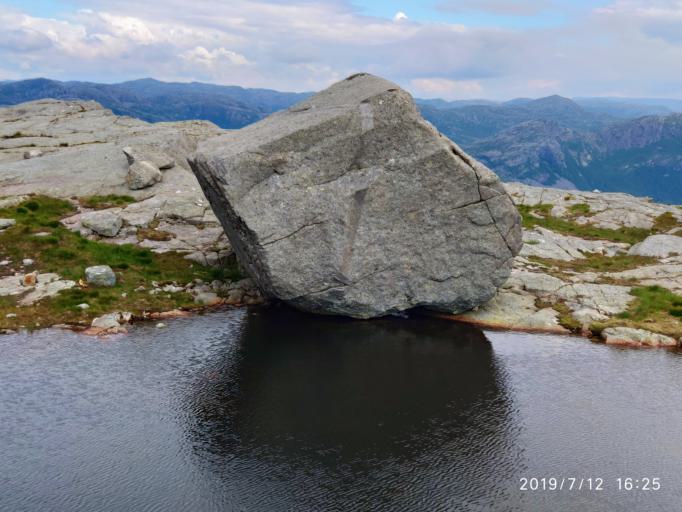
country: NO
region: Rogaland
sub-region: Forsand
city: Forsand
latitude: 58.9847
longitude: 6.1831
